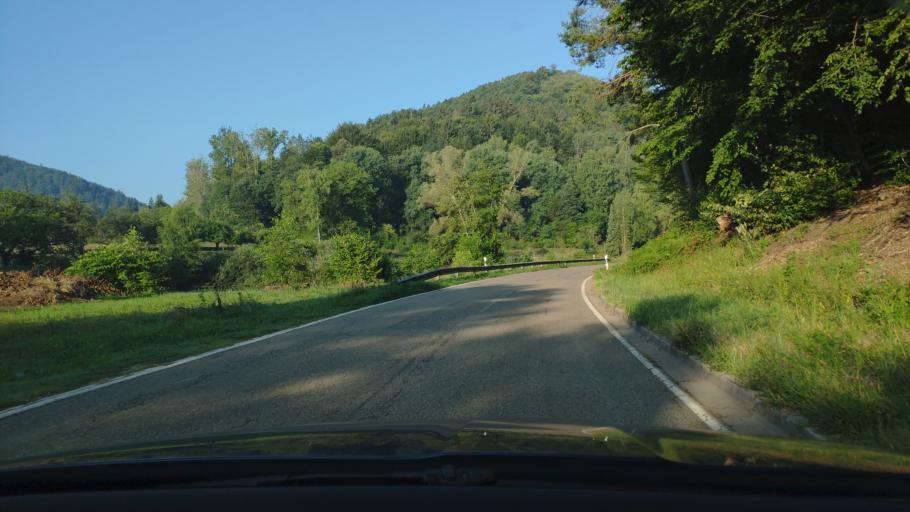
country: DE
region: Rheinland-Pfalz
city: Hirschthal
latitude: 49.0607
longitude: 7.7379
